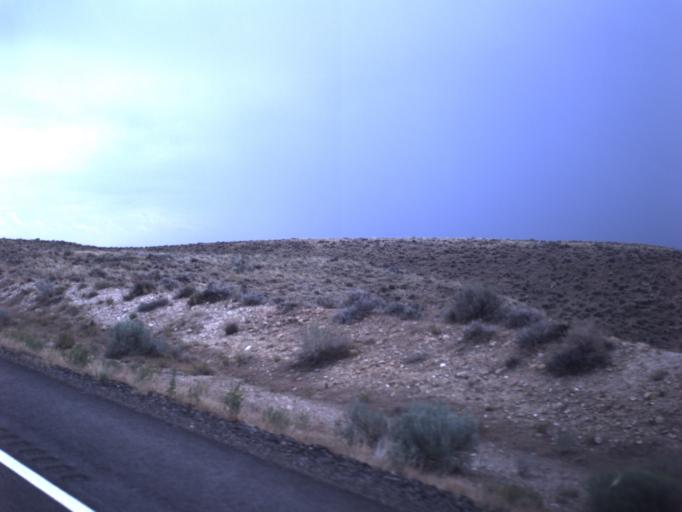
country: US
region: Utah
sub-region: Uintah County
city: Naples
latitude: 40.2786
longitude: -109.4662
